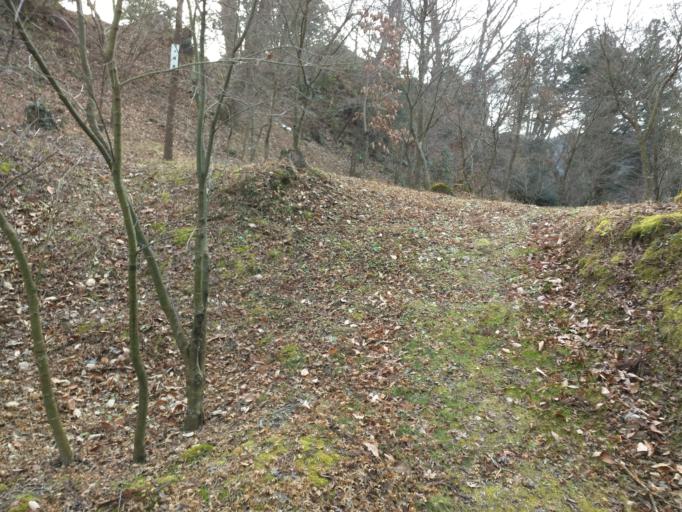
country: JP
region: Fukushima
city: Ishikawa
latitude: 37.1456
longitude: 140.4507
